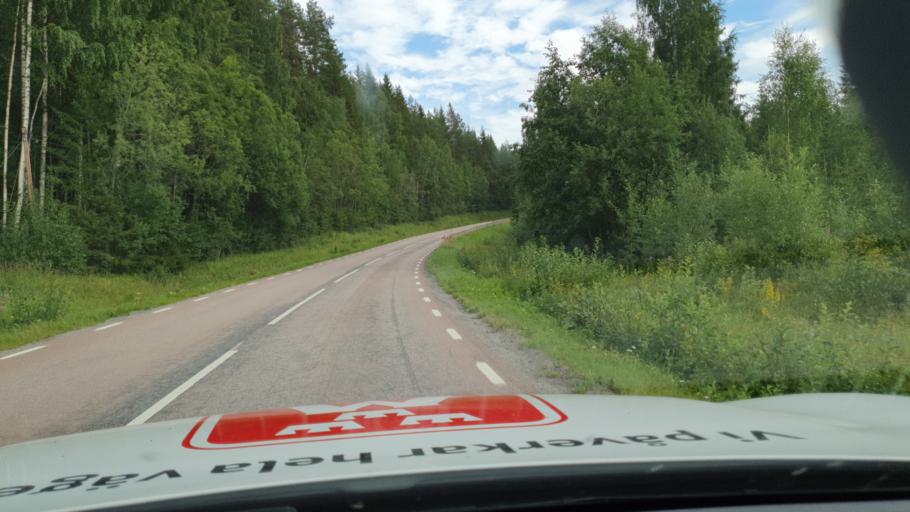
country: SE
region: Vaesternorrland
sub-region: Solleftea Kommun
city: As
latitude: 63.5694
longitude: 16.4270
